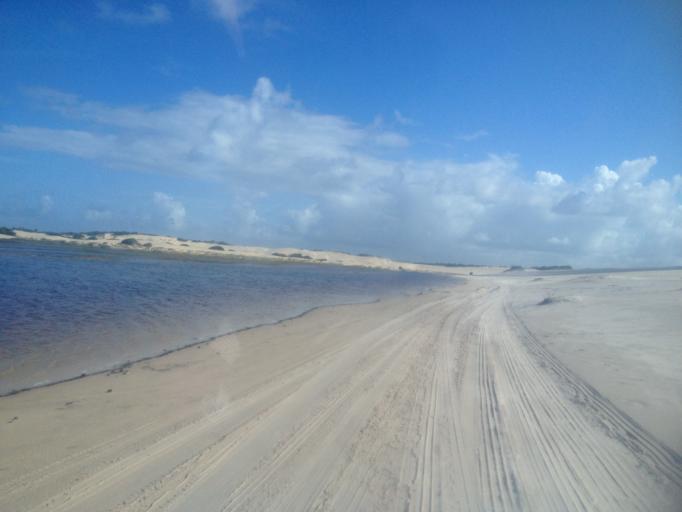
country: BR
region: Sergipe
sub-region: Indiaroba
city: Indiaroba
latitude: -11.4729
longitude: -37.3705
